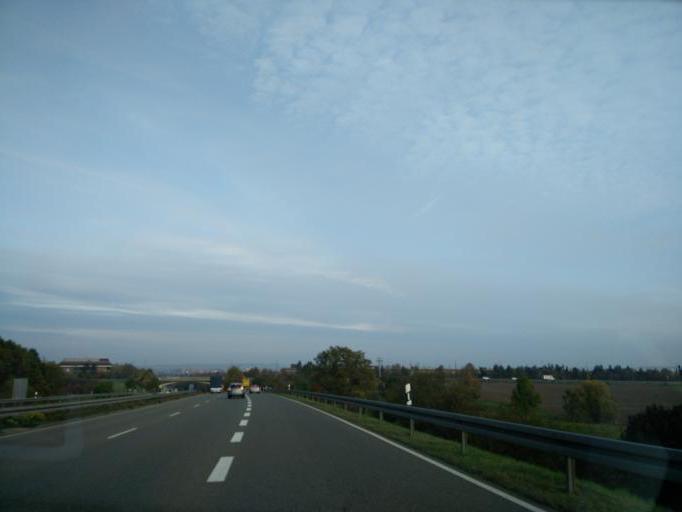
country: DE
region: Baden-Wuerttemberg
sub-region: Regierungsbezirk Stuttgart
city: Boeblingen
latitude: 48.6725
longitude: 8.9814
